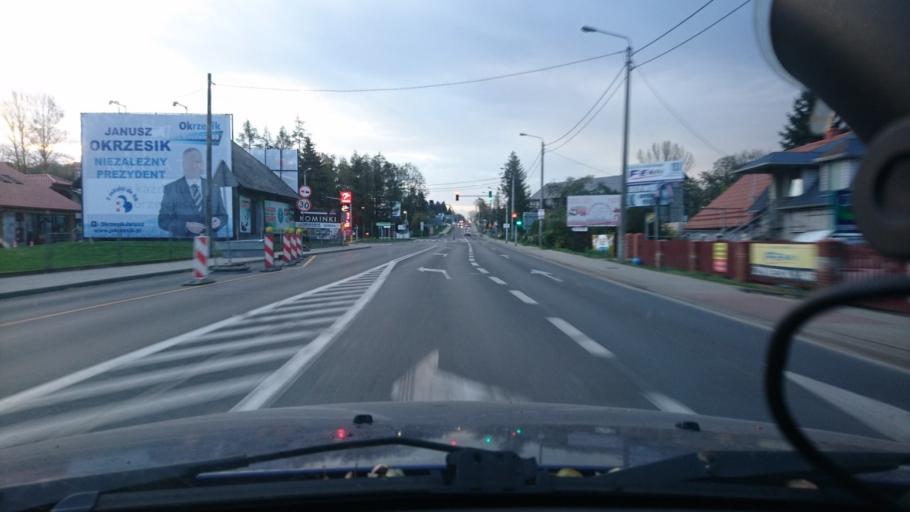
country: PL
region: Silesian Voivodeship
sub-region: Bielsko-Biala
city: Bielsko-Biala
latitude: 49.8007
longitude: 19.0603
